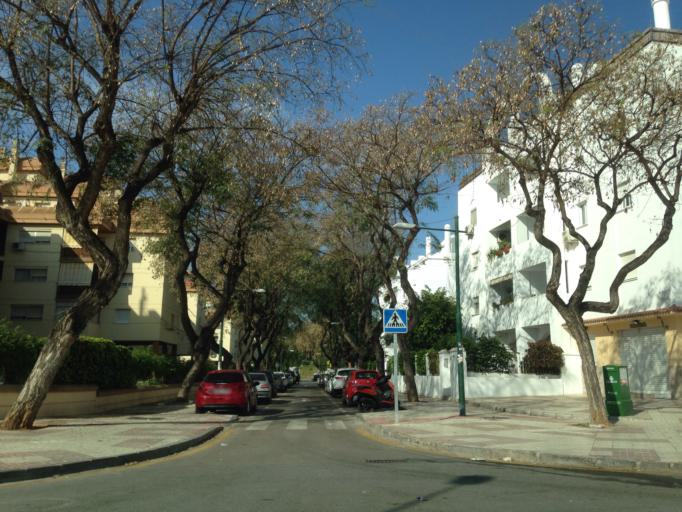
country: ES
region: Andalusia
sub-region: Provincia de Malaga
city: Malaga
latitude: 36.7218
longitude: -4.4823
